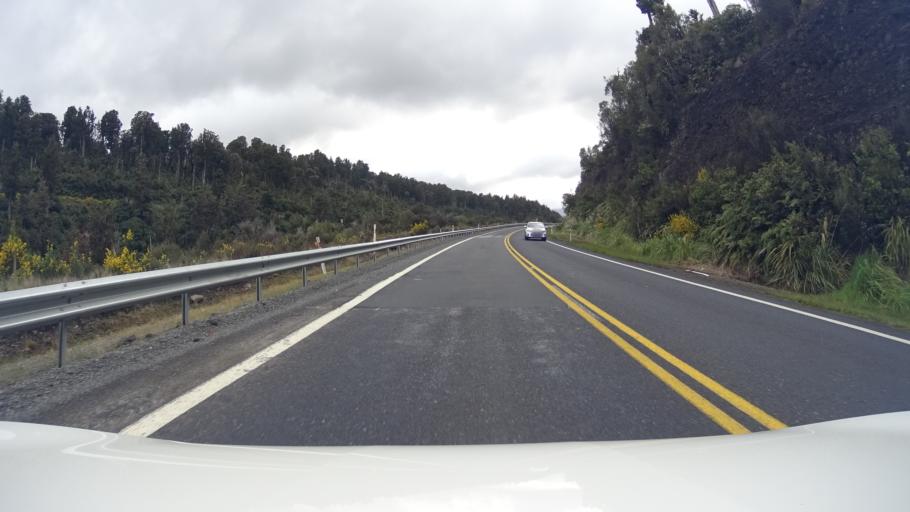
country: NZ
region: Manawatu-Wanganui
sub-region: Ruapehu District
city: Waiouru
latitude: -39.2652
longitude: 175.3940
